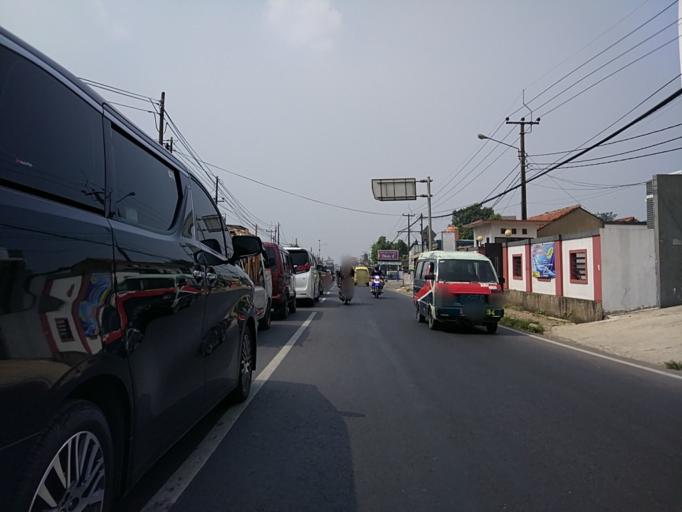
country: ID
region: West Java
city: Padalarang
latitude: -6.8353
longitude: 107.4700
